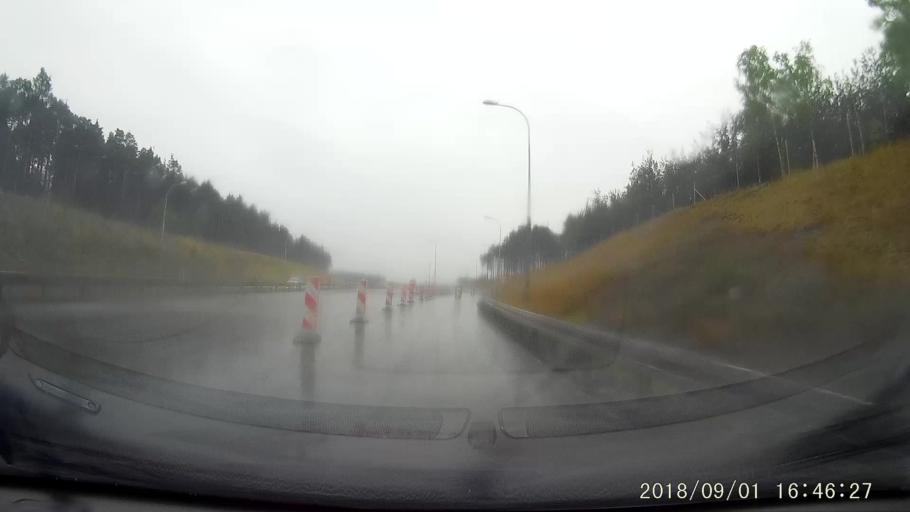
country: PL
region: Lubusz
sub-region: Zielona Gora
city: Zielona Gora
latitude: 51.9605
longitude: 15.5594
